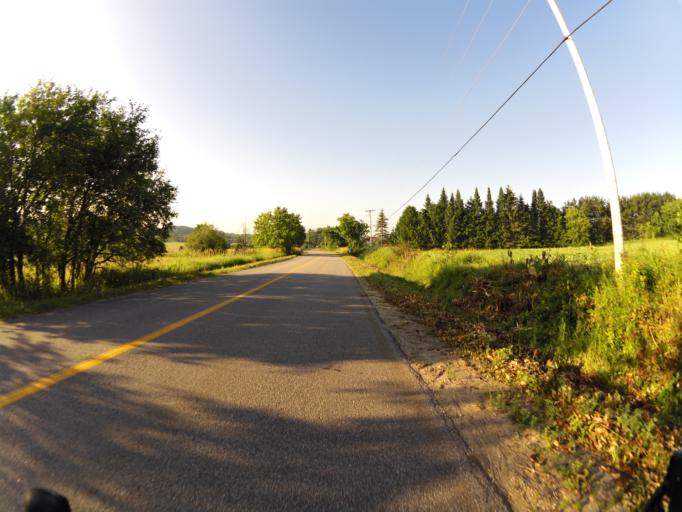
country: CA
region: Quebec
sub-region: Outaouais
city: Wakefield
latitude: 45.7230
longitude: -75.9697
